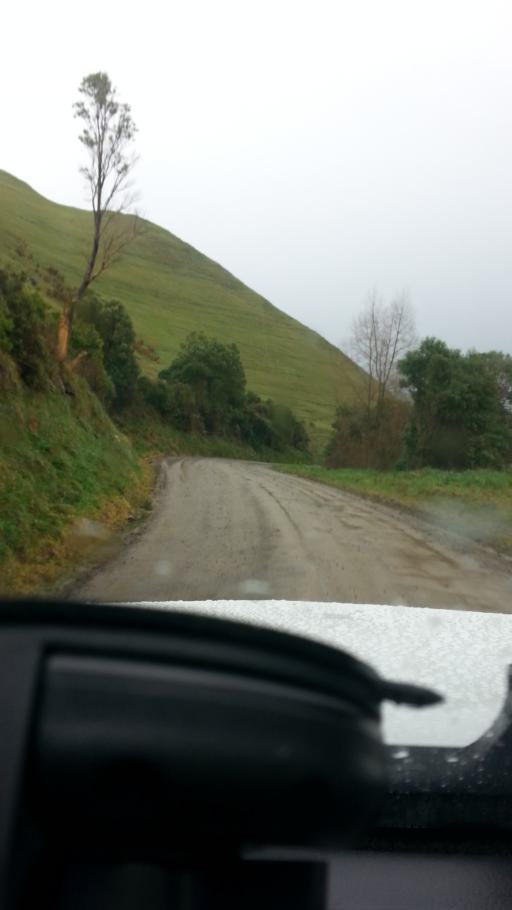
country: NZ
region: Wellington
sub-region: Masterton District
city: Masterton
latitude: -40.8114
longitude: 175.5831
